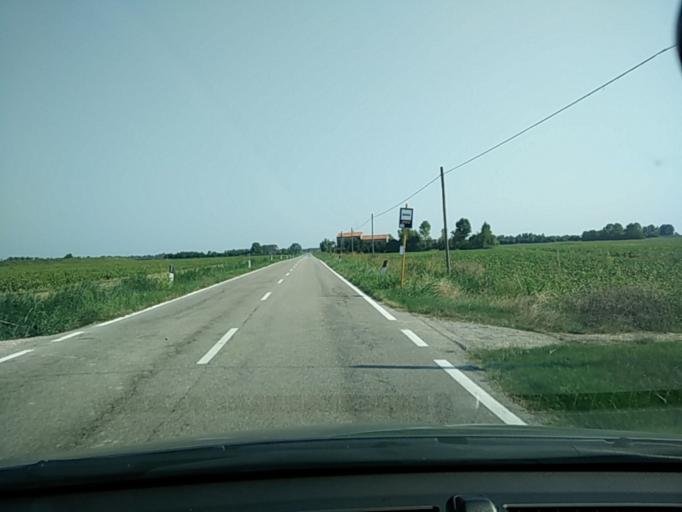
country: IT
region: Veneto
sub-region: Provincia di Venezia
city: La Salute di Livenza
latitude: 45.6362
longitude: 12.8310
